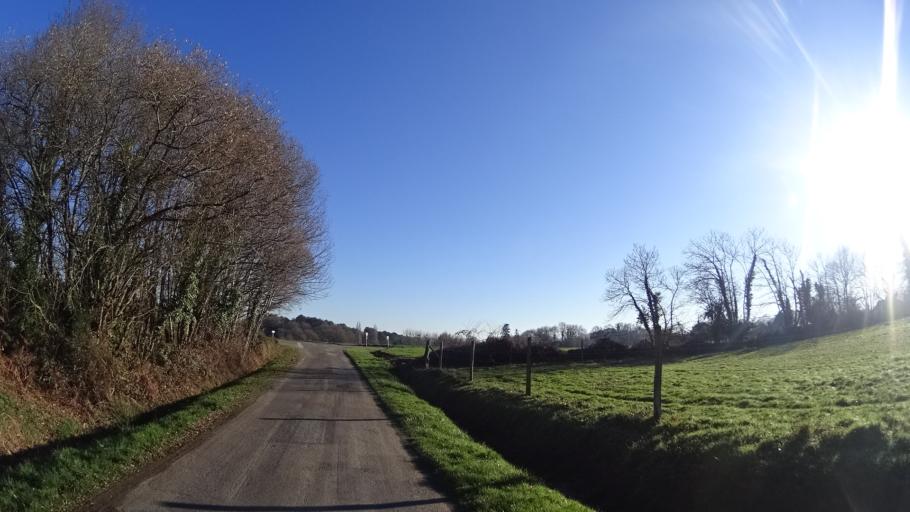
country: FR
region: Brittany
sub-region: Departement du Morbihan
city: Saint-Jean-la-Poterie
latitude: 47.6468
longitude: -2.1321
